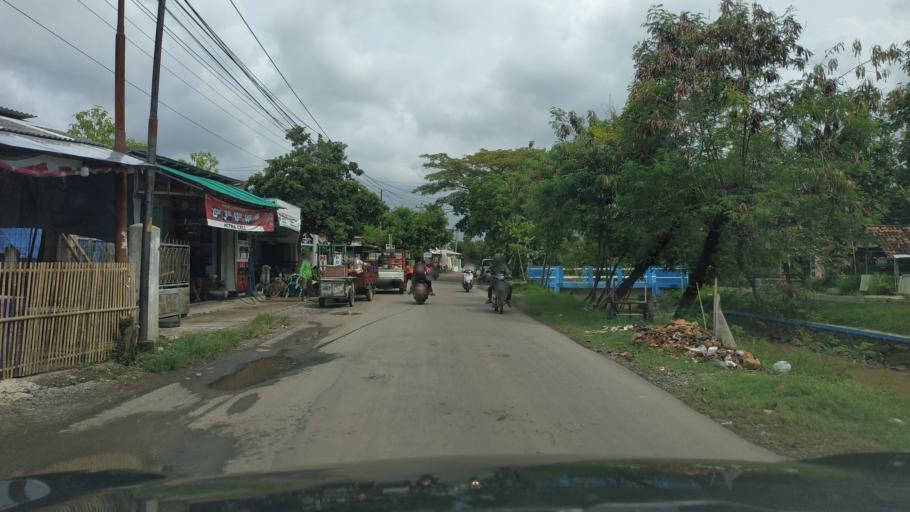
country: ID
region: Central Java
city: Pemalang
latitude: -6.9138
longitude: 109.3292
